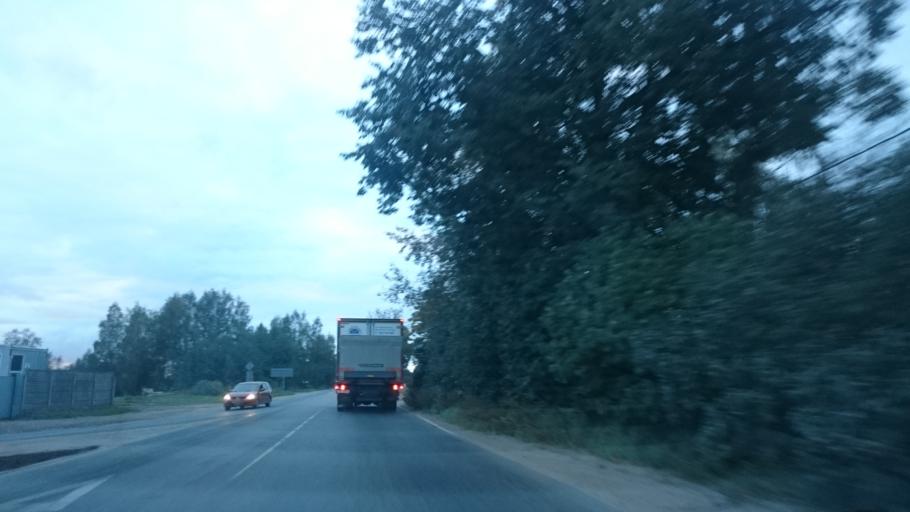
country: LV
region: Kekava
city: Kekava
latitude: 56.8983
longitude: 24.2306
